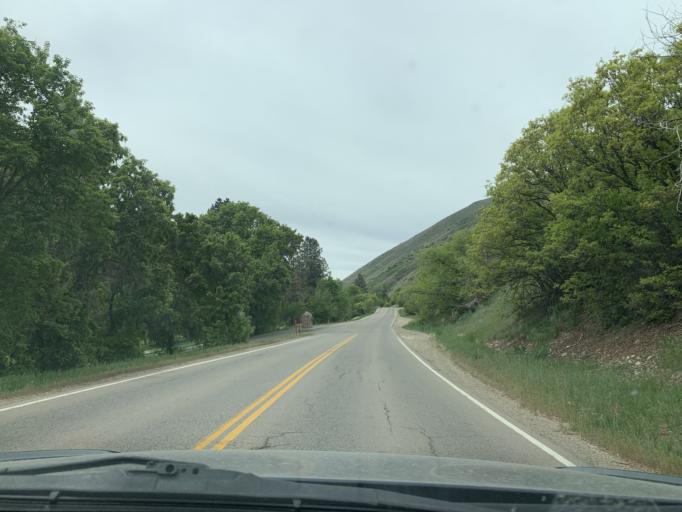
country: US
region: Utah
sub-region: Utah County
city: Mapleton
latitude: 40.1634
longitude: -111.5027
